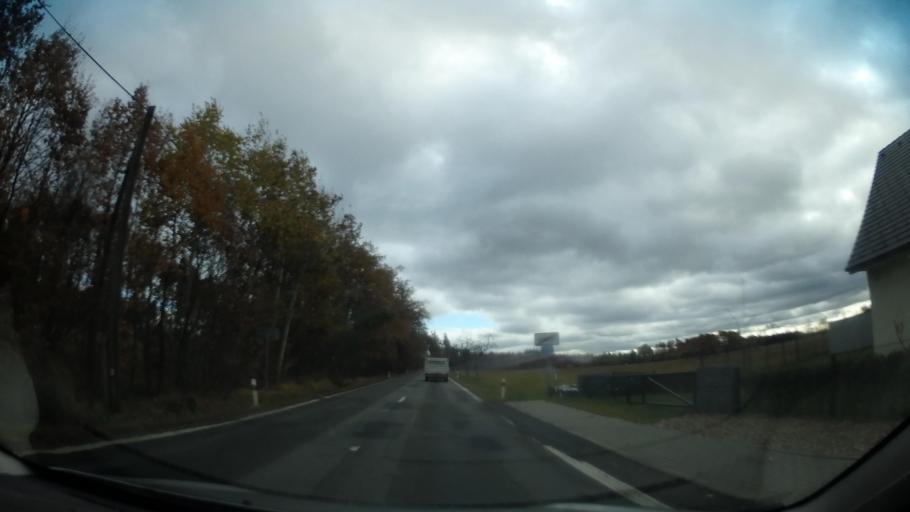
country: CZ
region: Vysocina
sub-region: Okres Zd'ar nad Sazavou
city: Velka Bites
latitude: 49.2670
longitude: 16.2432
